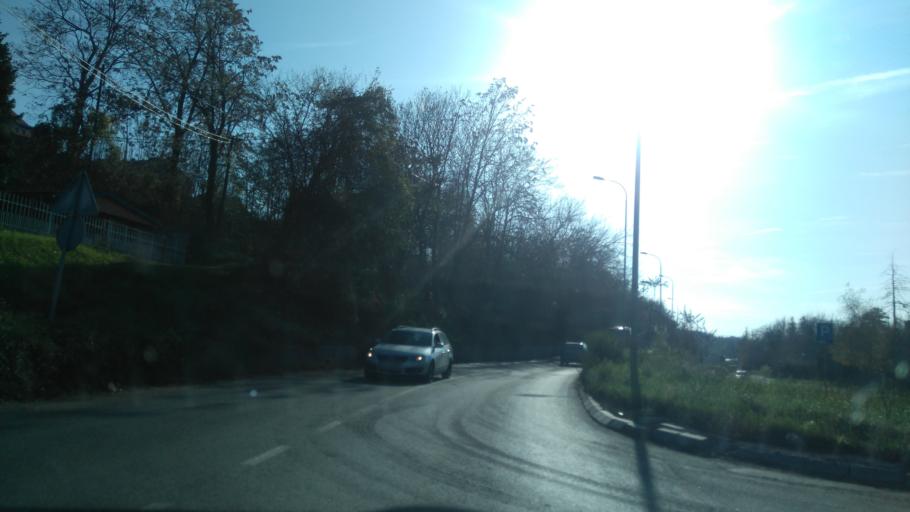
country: RS
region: Central Serbia
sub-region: Belgrade
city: Cukarica
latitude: 44.7535
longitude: 20.4033
